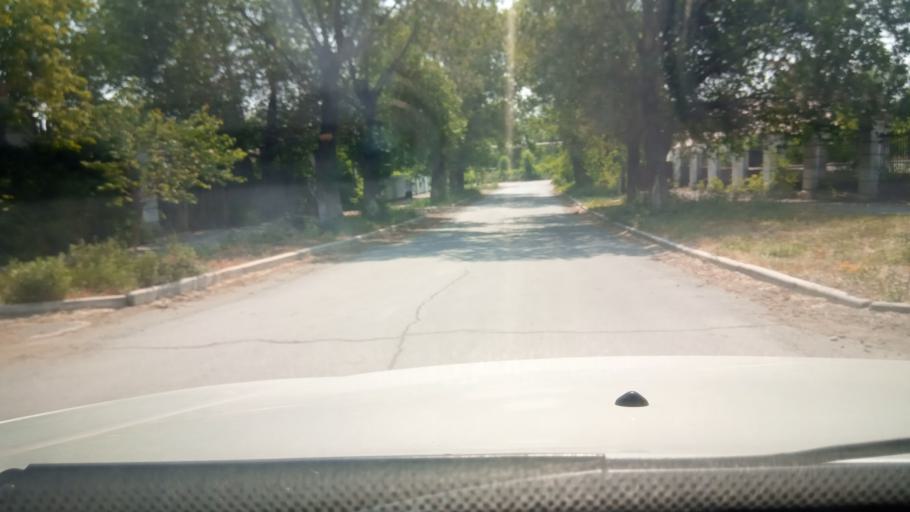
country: RU
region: Orenburg
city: Novotroitsk
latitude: 51.1955
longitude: 58.3324
